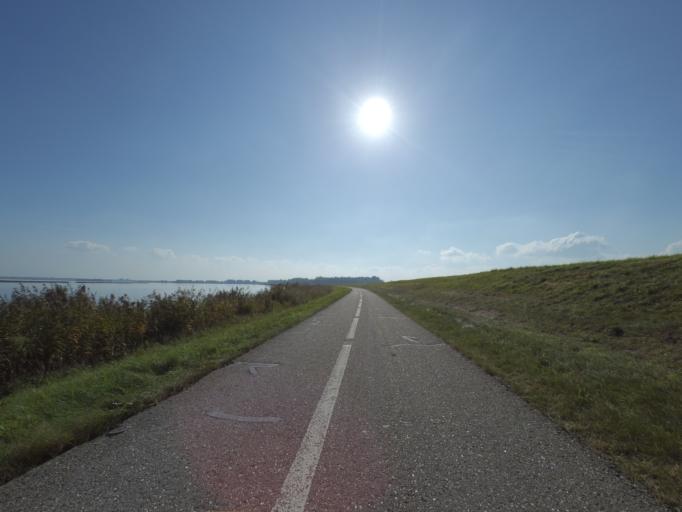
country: NL
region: Flevoland
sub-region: Gemeente Zeewolde
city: Zeewolde
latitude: 52.3481
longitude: 5.5372
